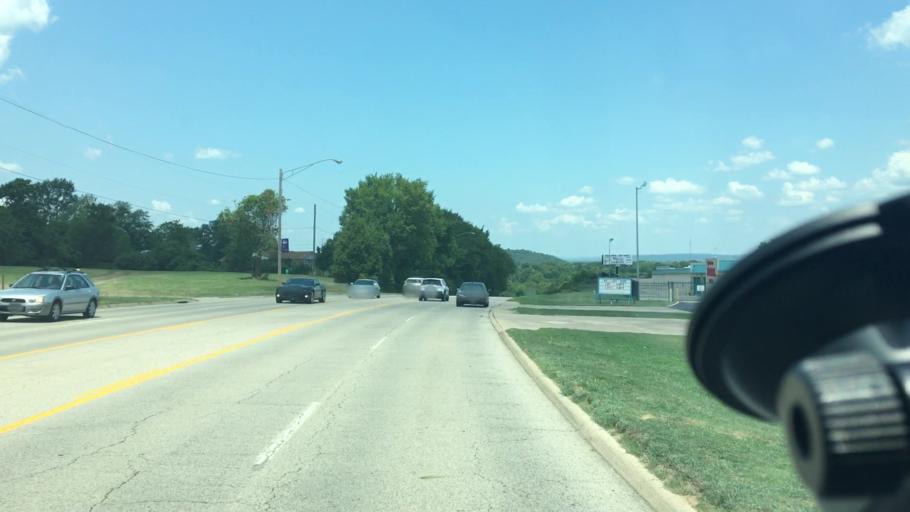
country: US
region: Arkansas
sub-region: Sebastian County
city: Barling
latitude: 35.3377
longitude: -94.3190
